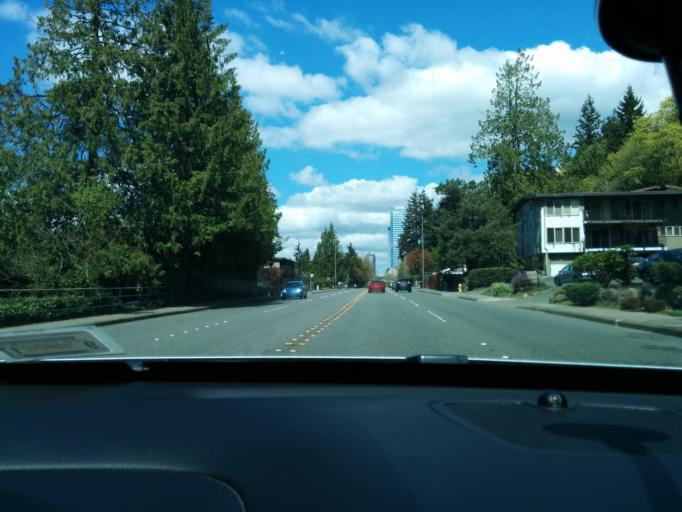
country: US
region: Washington
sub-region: King County
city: Bellevue
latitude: 47.6044
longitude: -122.2014
